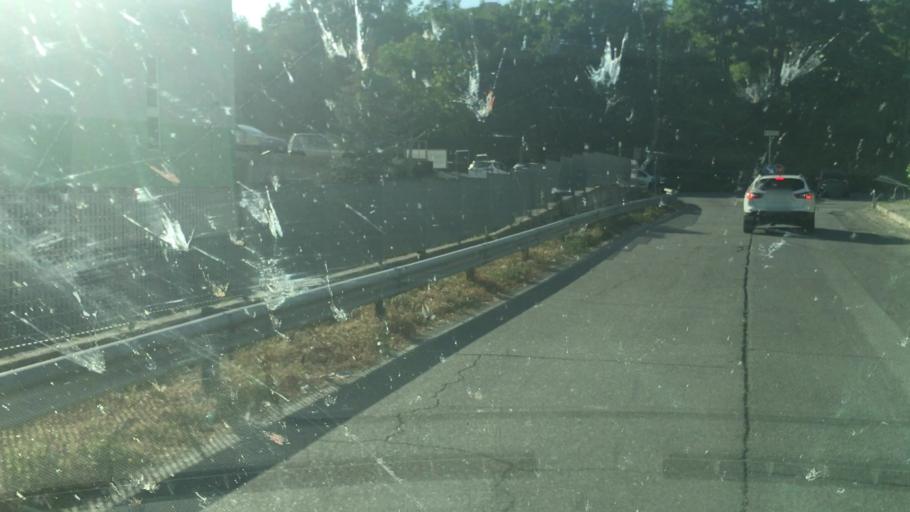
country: IT
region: Basilicate
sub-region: Provincia di Potenza
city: Potenza
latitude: 40.6342
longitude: 15.8168
